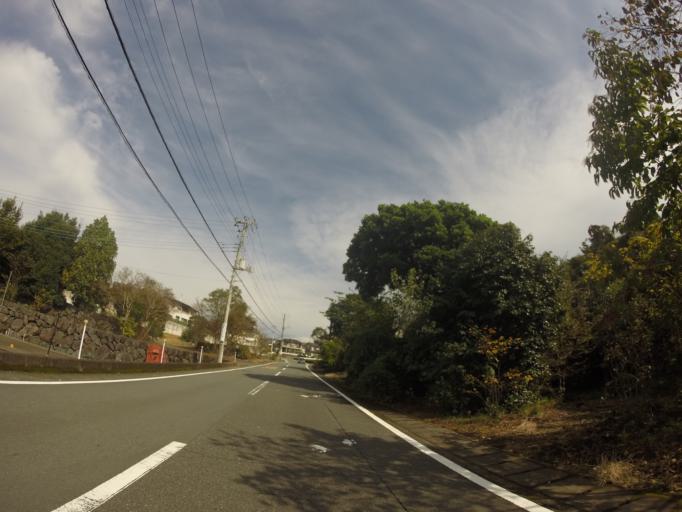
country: JP
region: Shizuoka
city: Fuji
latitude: 35.1903
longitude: 138.6928
